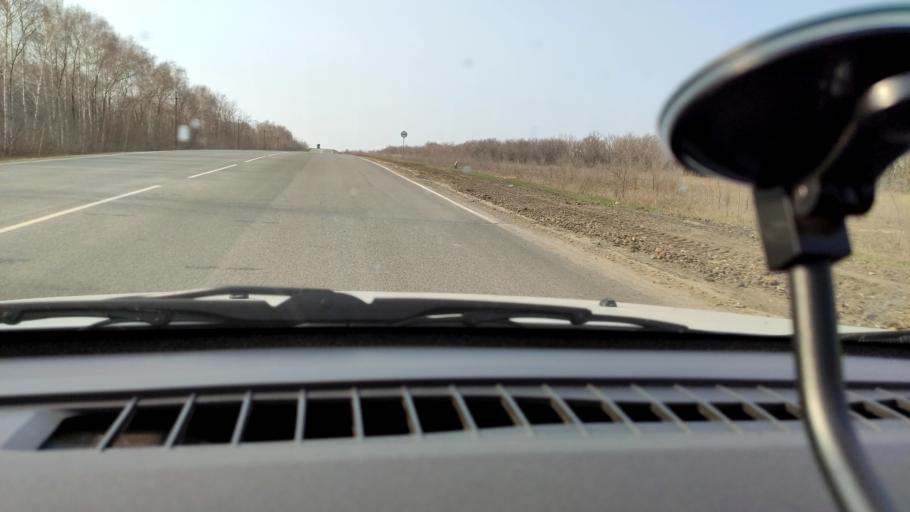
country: RU
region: Samara
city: Dubovyy Umet
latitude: 53.0725
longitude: 50.3597
